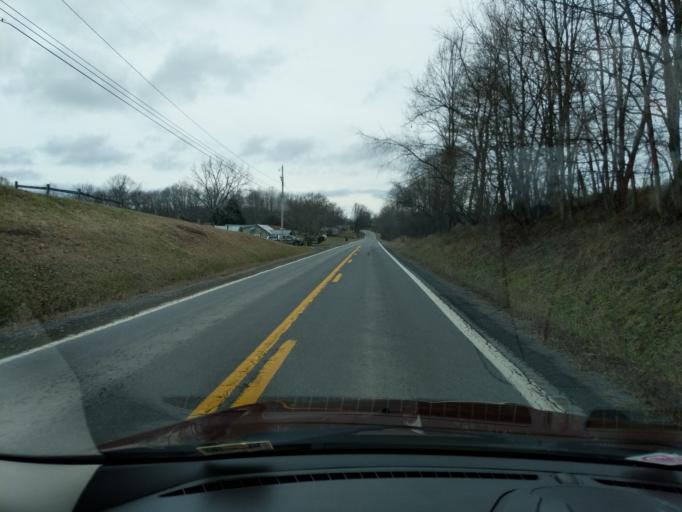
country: US
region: West Virginia
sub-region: Greenbrier County
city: Lewisburg
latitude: 37.8455
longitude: -80.5516
